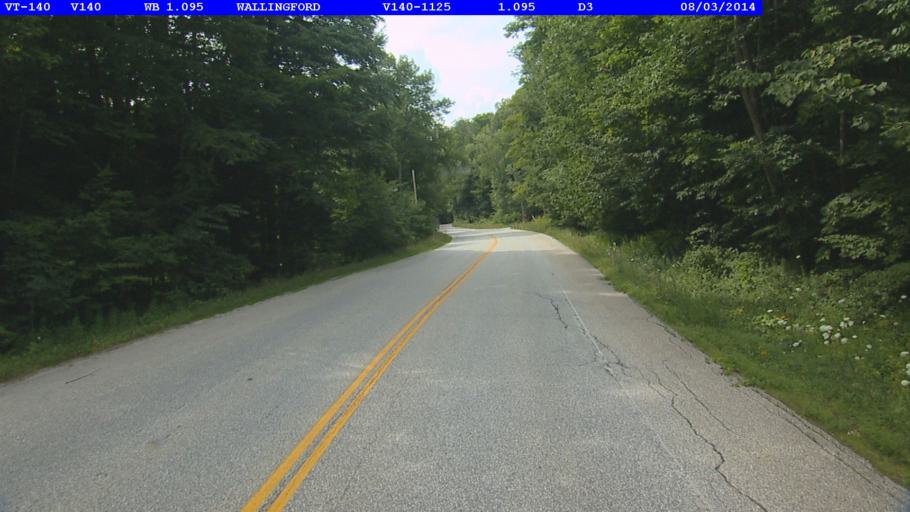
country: US
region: Vermont
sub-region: Rutland County
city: Rutland
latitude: 43.4660
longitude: -72.9578
